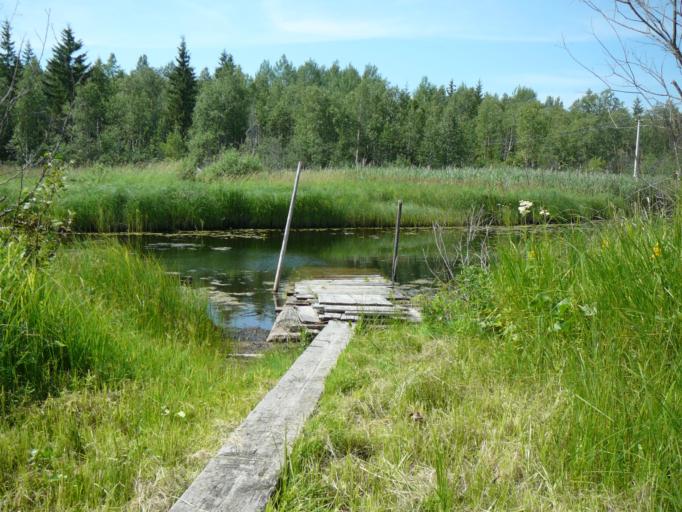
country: RU
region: Vologda
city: Ust'ye
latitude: 60.1577
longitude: 39.5486
